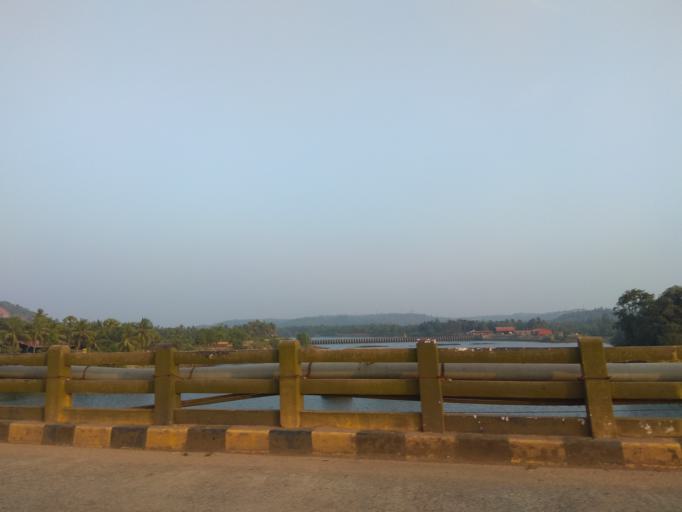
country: IN
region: Karnataka
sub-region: Dakshina Kannada
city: Mangalore
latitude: 12.9409
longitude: 74.8659
